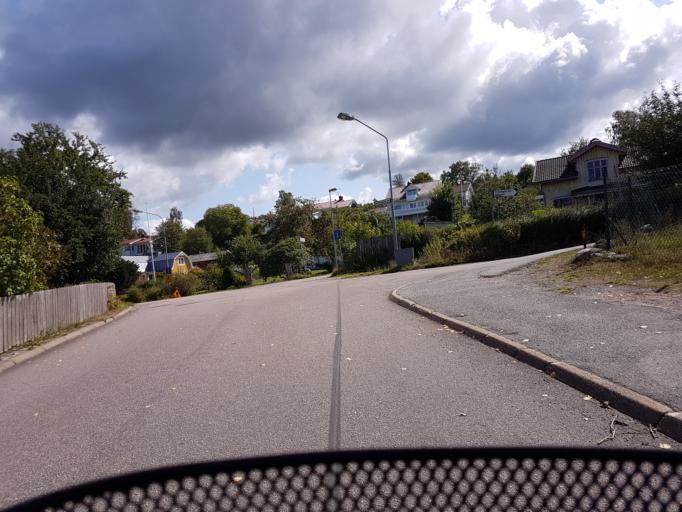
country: SE
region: Vaestra Goetaland
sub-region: Ale Kommun
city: Alvangen
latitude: 57.9591
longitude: 12.1299
